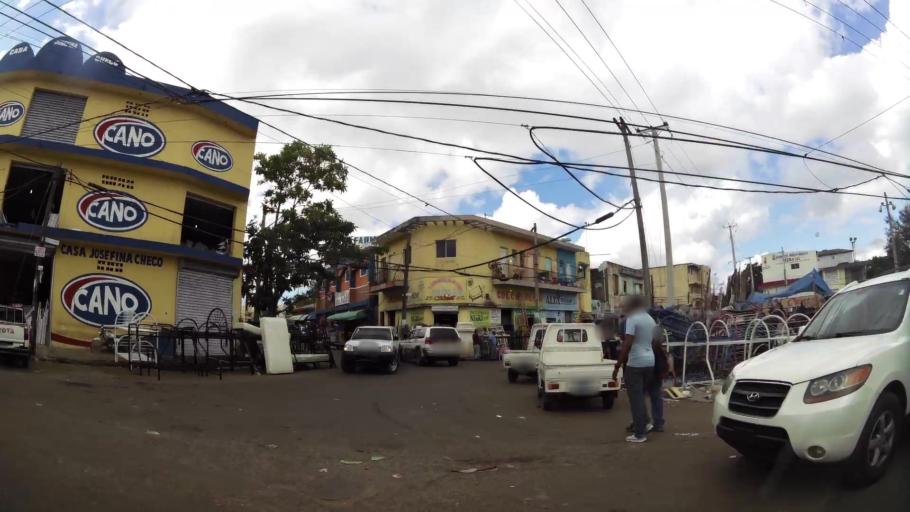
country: DO
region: Nacional
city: San Carlos
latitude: 18.4884
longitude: -69.8976
